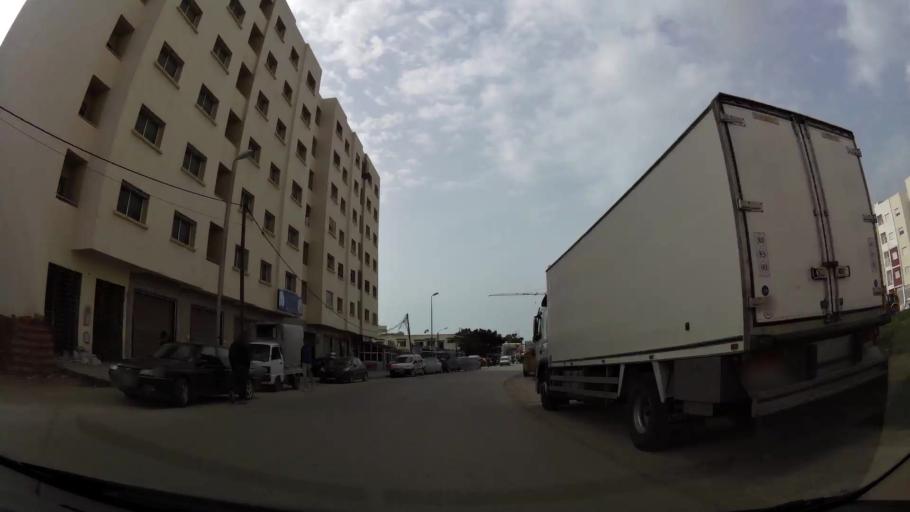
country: MA
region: Tanger-Tetouan
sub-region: Tanger-Assilah
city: Boukhalef
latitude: 35.7067
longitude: -5.9055
